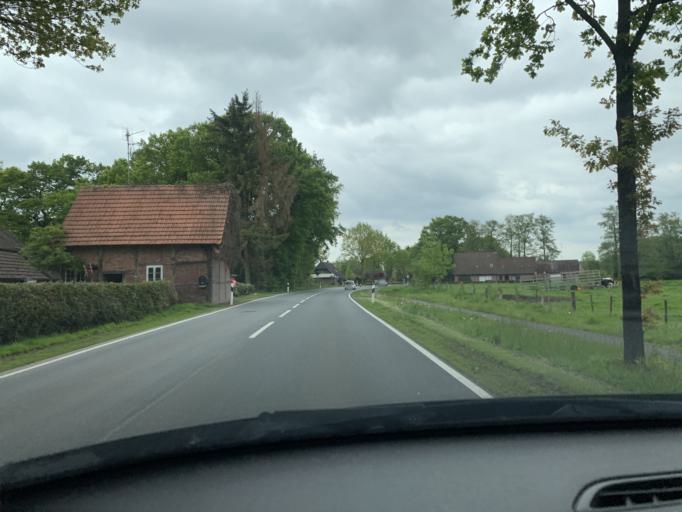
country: DE
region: Lower Saxony
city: Bad Zwischenahn
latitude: 53.2168
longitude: 8.0093
